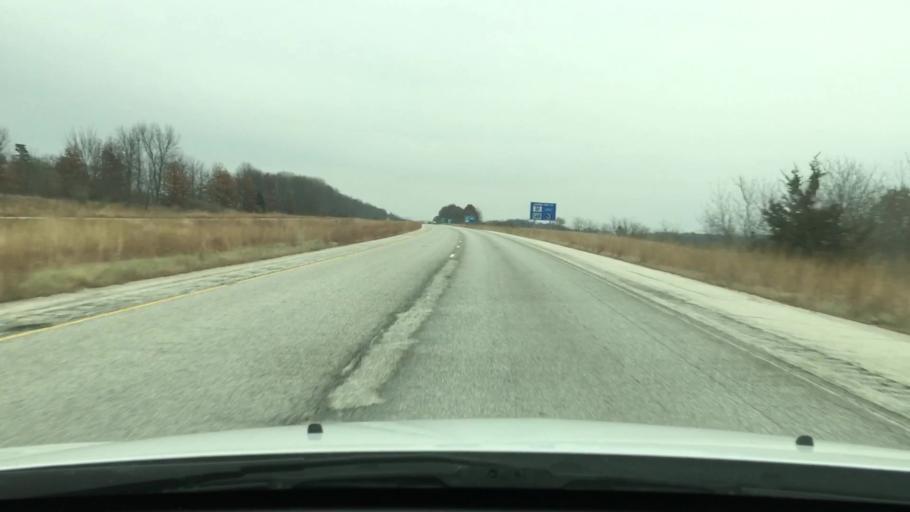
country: US
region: Illinois
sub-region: Morgan County
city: South Jacksonville
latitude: 39.6809
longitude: -90.2635
